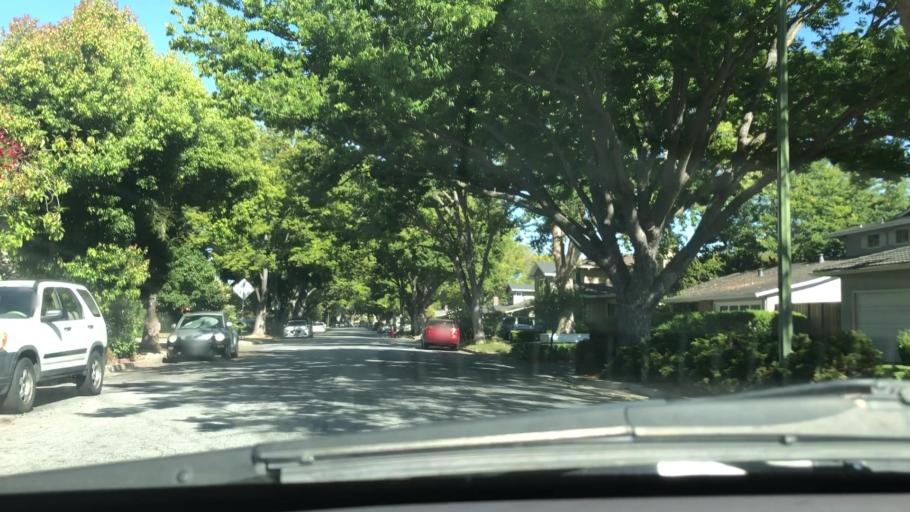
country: US
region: California
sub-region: Santa Clara County
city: Campbell
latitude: 37.2981
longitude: -121.9890
